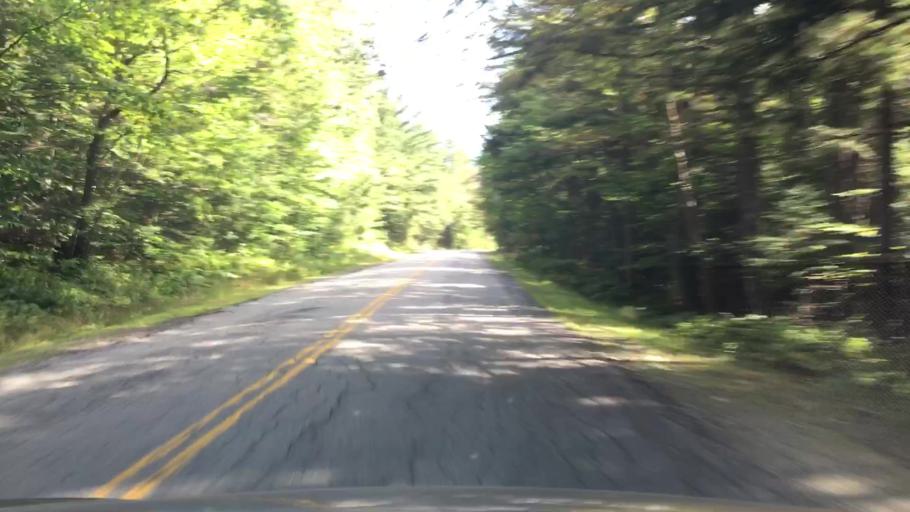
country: US
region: New Hampshire
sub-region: Carroll County
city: Tamworth
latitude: 44.0063
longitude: -71.3209
